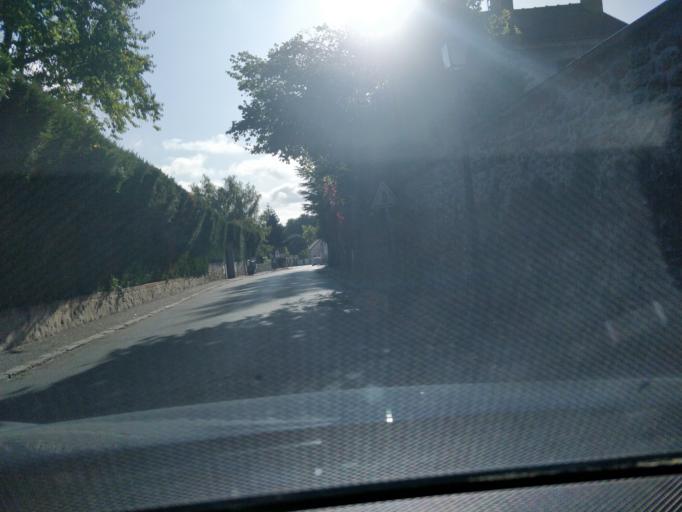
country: FR
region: Ile-de-France
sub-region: Departement de l'Essonne
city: Vaugrigneuse
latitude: 48.6027
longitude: 2.1196
